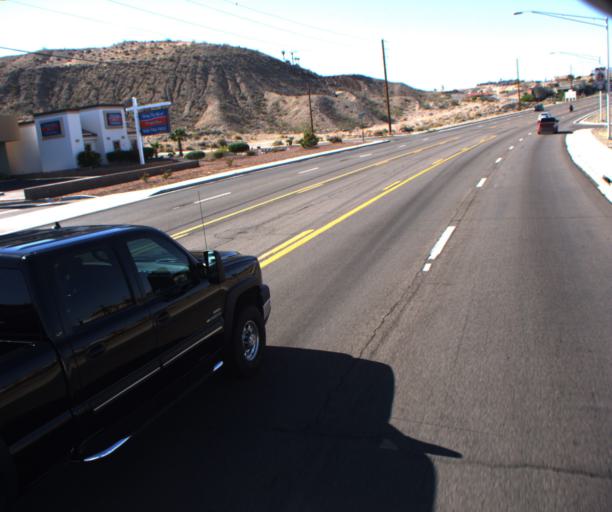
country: US
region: Arizona
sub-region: Mohave County
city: Bullhead City
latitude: 35.0486
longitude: -114.5890
